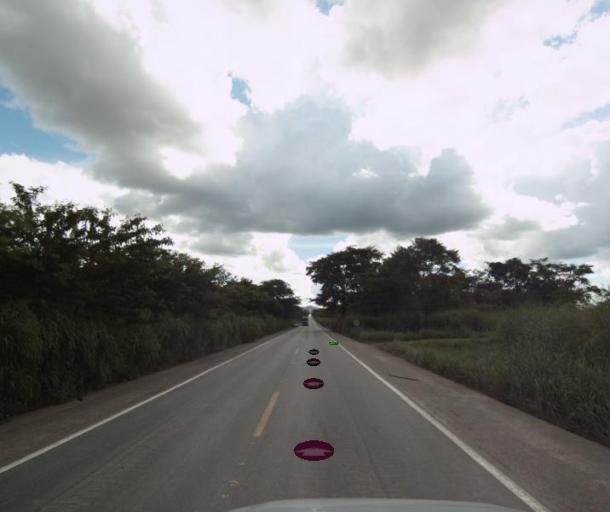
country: BR
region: Goias
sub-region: Porangatu
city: Porangatu
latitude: -13.5546
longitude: -49.0762
